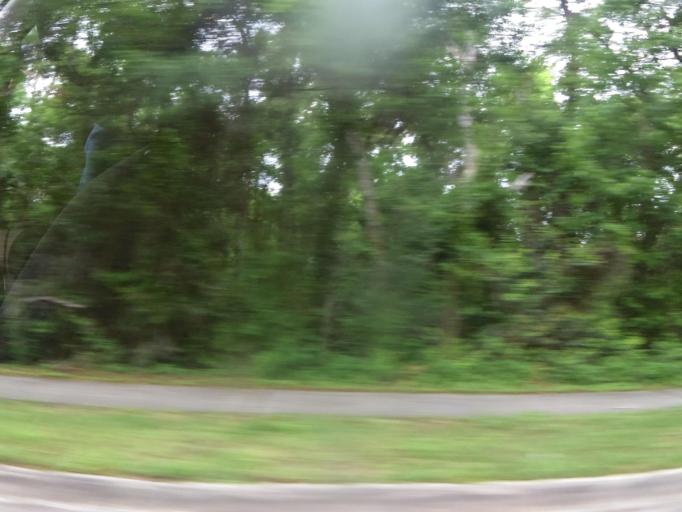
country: US
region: Florida
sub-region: Clay County
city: Bellair-Meadowbrook Terrace
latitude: 30.2853
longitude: -81.7680
